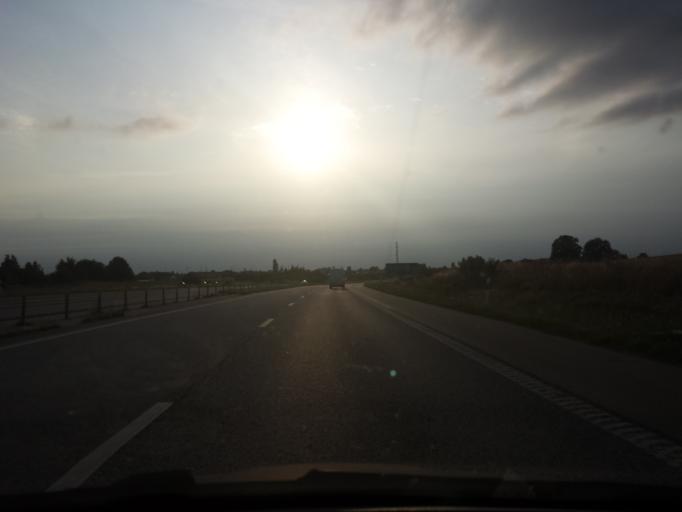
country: SE
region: Skane
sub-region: Svedala Kommun
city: Svedala
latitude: 55.5147
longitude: 13.2577
